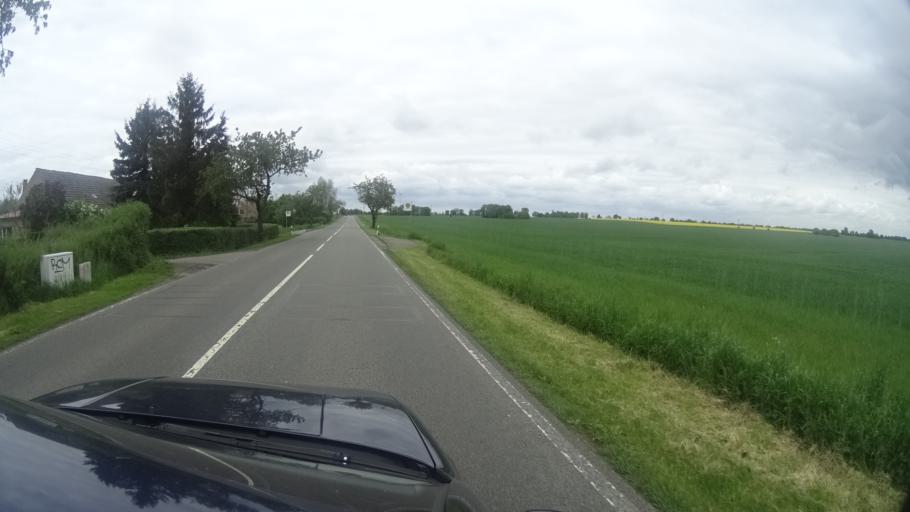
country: DE
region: Brandenburg
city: Fehrbellin
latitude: 52.8575
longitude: 12.7774
